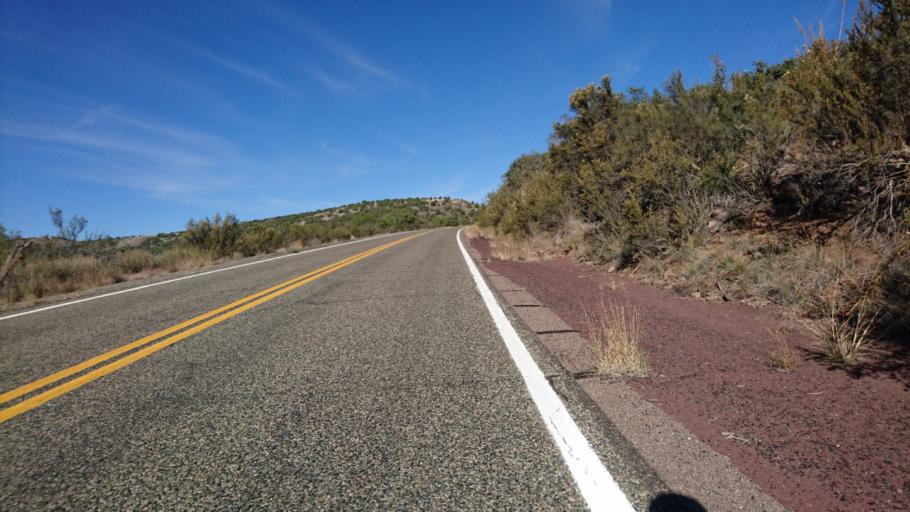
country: US
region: Arizona
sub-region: Yavapai County
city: Paulden
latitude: 35.2733
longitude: -112.6867
